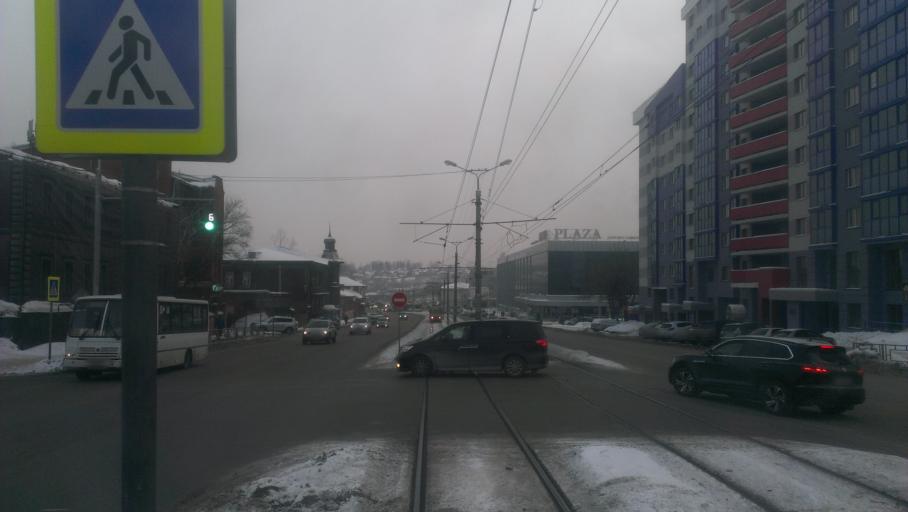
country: RU
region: Altai Krai
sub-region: Gorod Barnaulskiy
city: Barnaul
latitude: 53.3324
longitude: 83.7805
